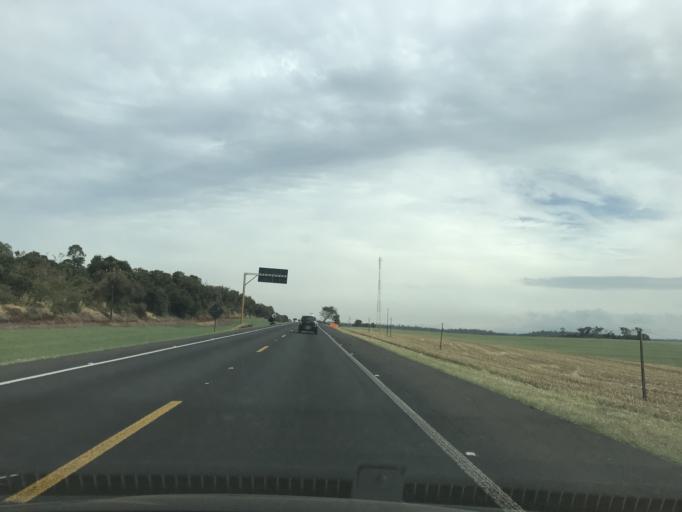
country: BR
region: Parana
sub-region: Matelandia
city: Matelandia
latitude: -25.0929
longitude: -53.7318
